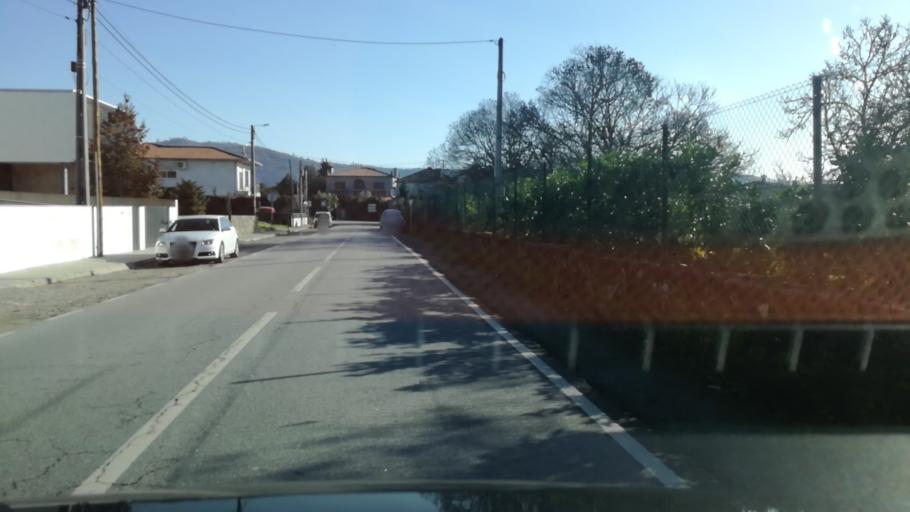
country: PT
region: Braga
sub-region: Guimaraes
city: Ponte
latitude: 41.5156
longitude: -8.3133
